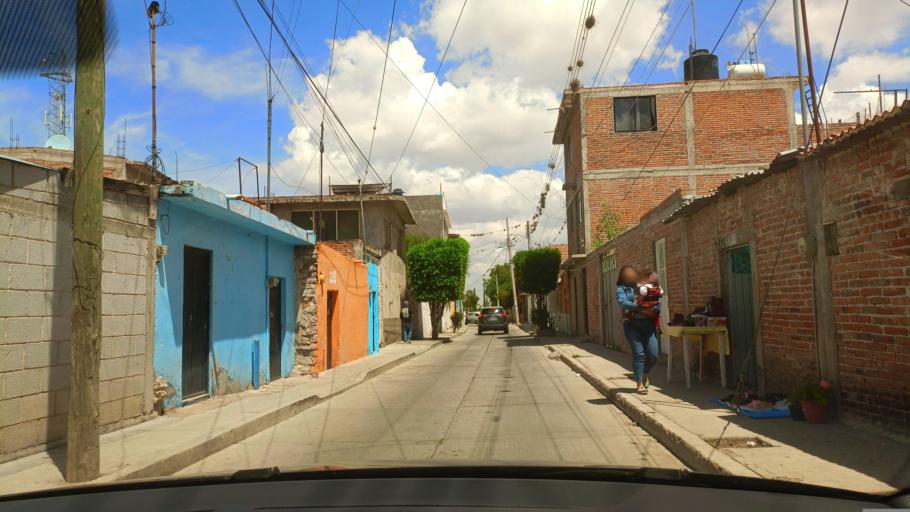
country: MX
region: Guanajuato
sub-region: San Luis de la Paz
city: San Luis de la Paz
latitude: 21.3026
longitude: -100.5177
